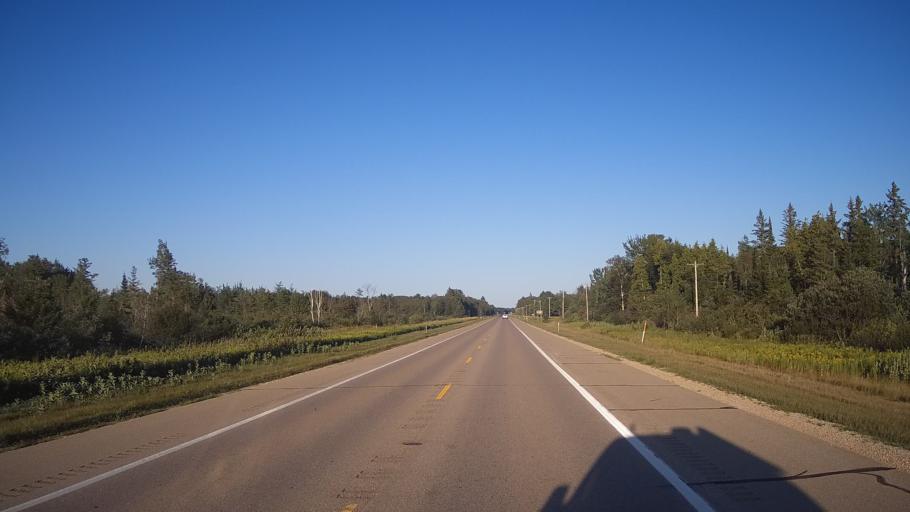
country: US
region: Michigan
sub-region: Delta County
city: Gladstone
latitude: 45.8955
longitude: -86.7301
